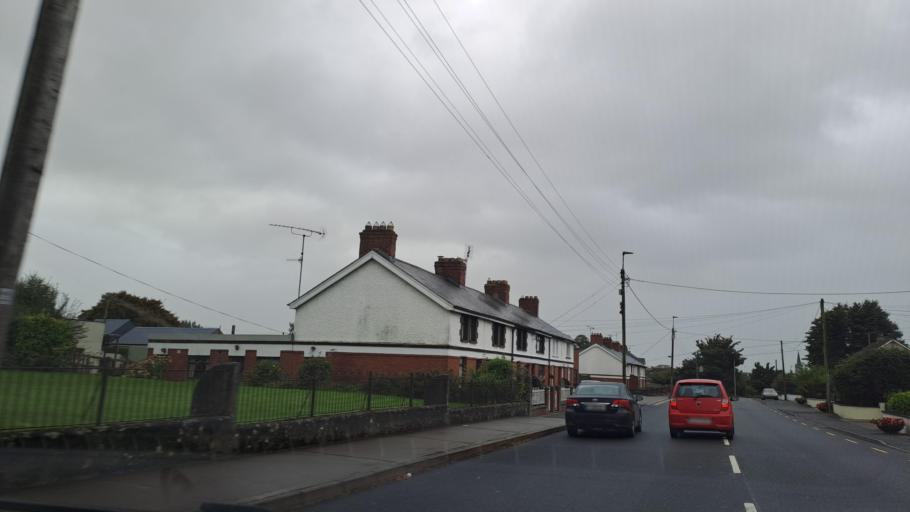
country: IE
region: Ulster
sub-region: County Monaghan
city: Carrickmacross
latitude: 53.9799
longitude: -6.7173
